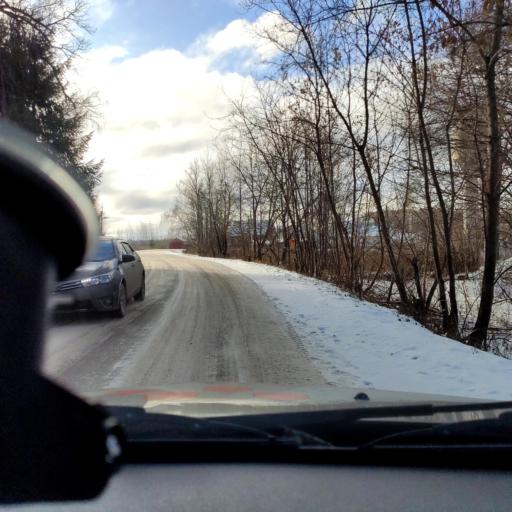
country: RU
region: Bashkortostan
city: Avdon
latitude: 54.7799
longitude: 55.7556
